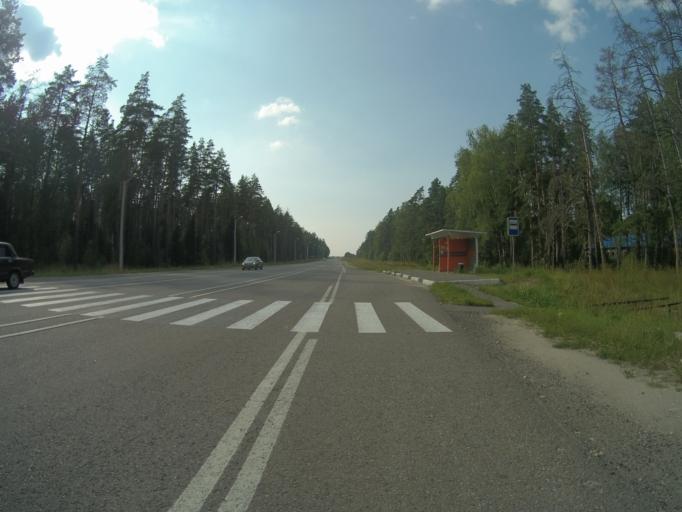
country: RU
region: Vladimir
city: Andreyevo
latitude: 55.9311
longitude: 41.1105
